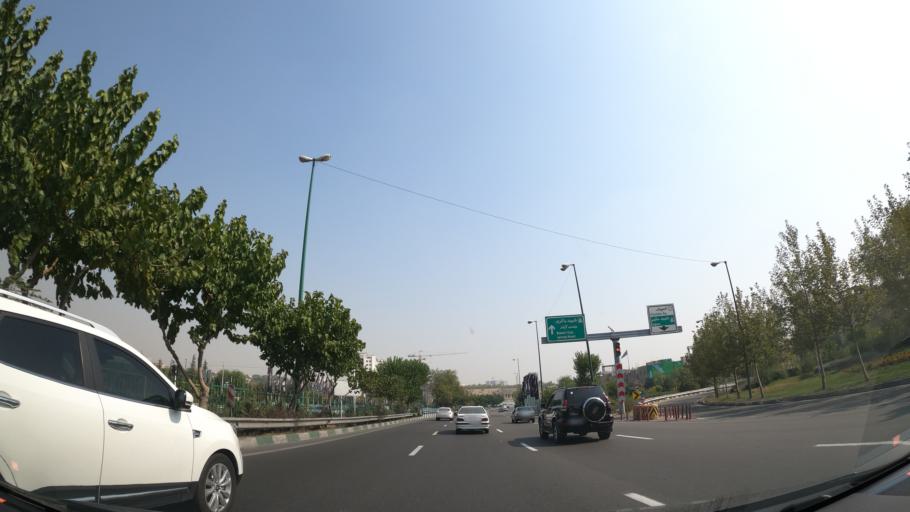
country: IR
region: Tehran
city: Shahr-e Qods
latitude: 35.7572
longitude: 51.2650
